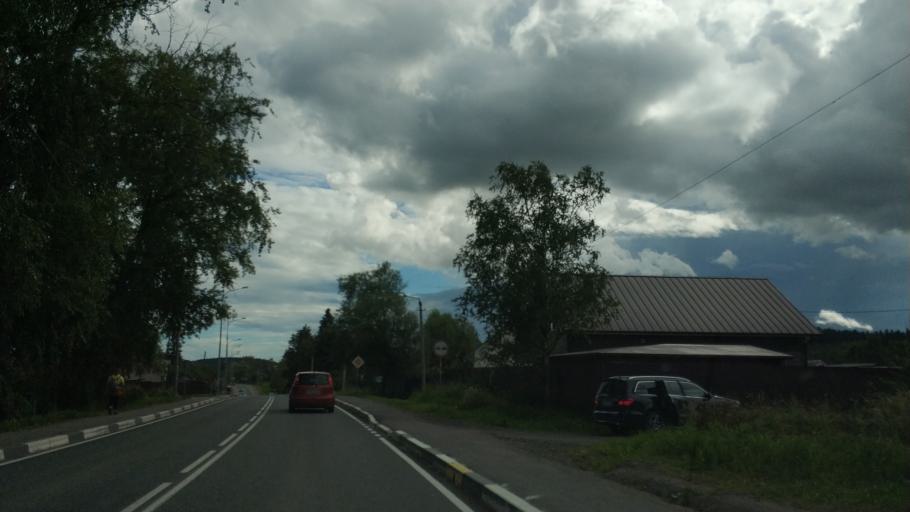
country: RU
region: Republic of Karelia
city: Khelyulya
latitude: 61.7507
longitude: 30.6619
